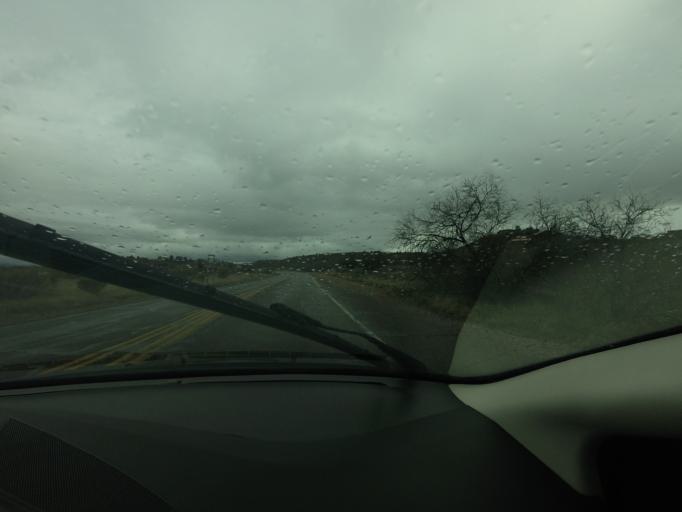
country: US
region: Arizona
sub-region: Yavapai County
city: Clarkdale
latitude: 34.7657
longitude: -112.0453
